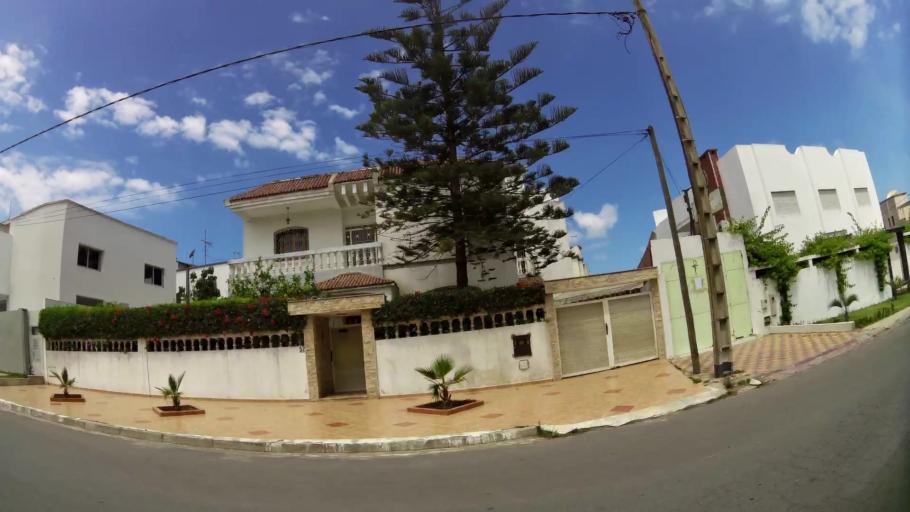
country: MA
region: Gharb-Chrarda-Beni Hssen
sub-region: Kenitra Province
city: Kenitra
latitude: 34.2682
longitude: -6.5963
